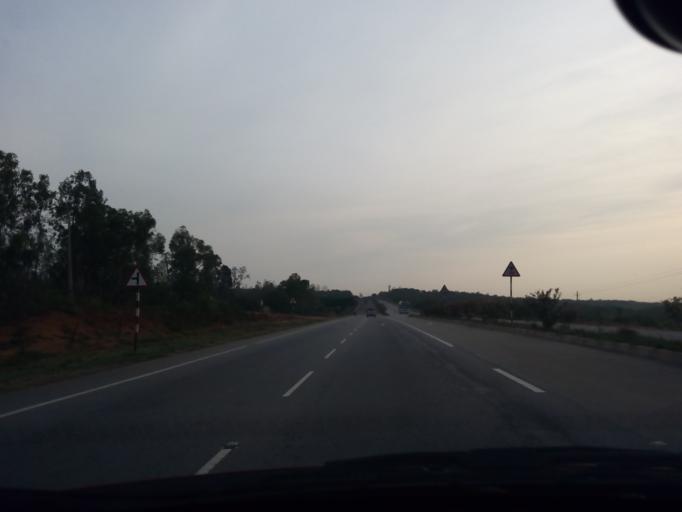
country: IN
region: Karnataka
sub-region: Chikkaballapur
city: Chik Ballapur
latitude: 13.5469
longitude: 77.7735
